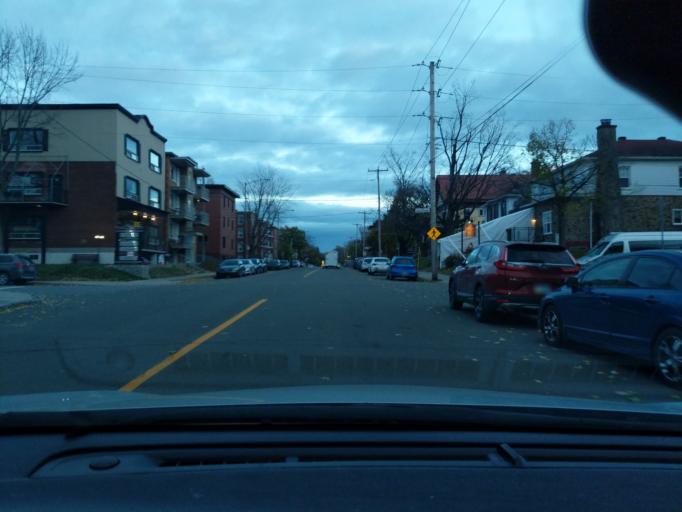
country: CA
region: Quebec
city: Quebec
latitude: 46.7935
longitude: -71.2554
